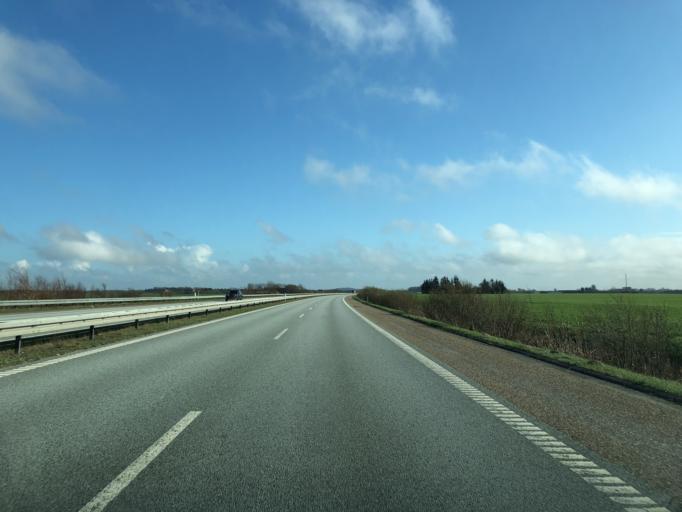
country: DK
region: North Denmark
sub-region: Hjorring Kommune
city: Hjorring
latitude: 57.4746
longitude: 10.0429
